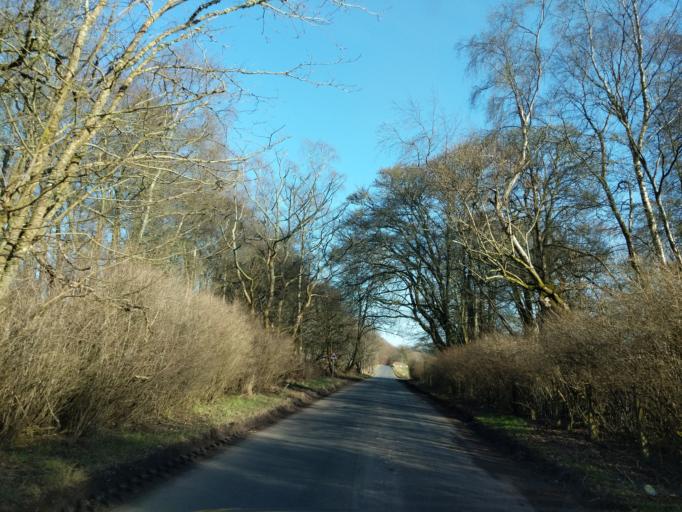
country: GB
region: Scotland
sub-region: The Scottish Borders
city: West Linton
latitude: 55.7185
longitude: -3.4256
